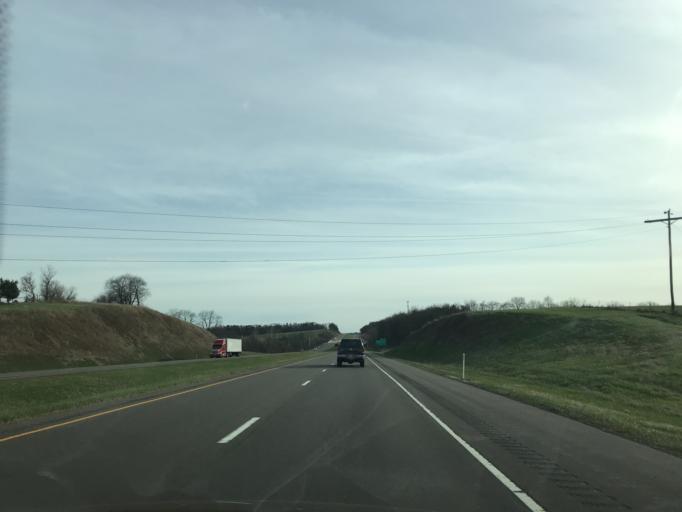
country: US
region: Pennsylvania
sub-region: Northumberland County
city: Watsontown
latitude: 41.0811
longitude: -76.8222
